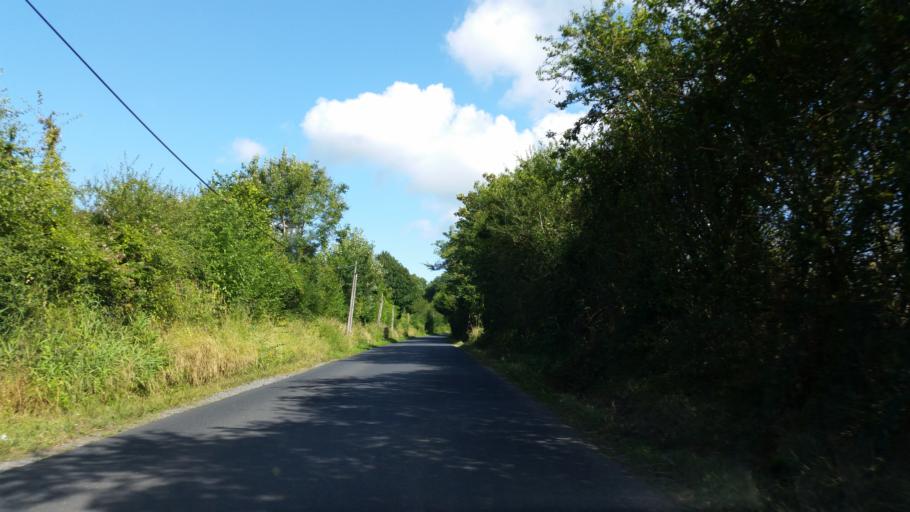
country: FR
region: Lower Normandy
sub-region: Departement du Calvados
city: Touques
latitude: 49.3392
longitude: 0.1126
